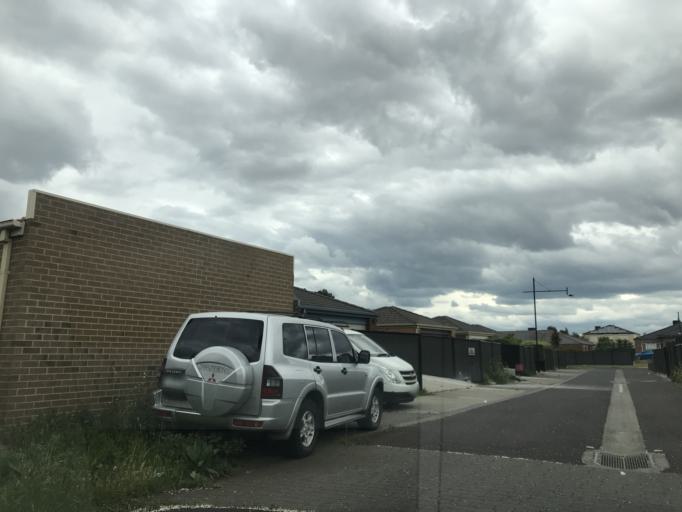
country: AU
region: Victoria
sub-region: Brimbank
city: Derrimut
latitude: -37.7937
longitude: 144.7668
